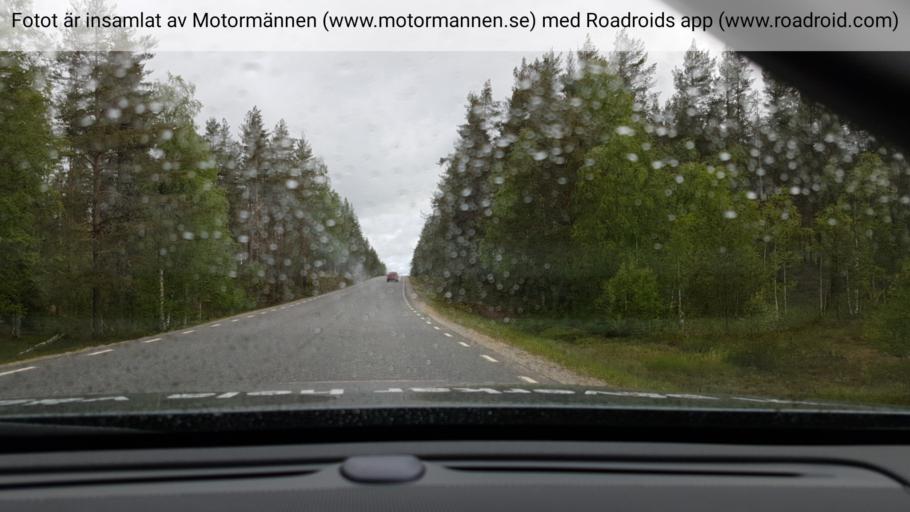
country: SE
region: Vaesterbotten
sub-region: Bjurholms Kommun
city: Bjurholm
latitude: 63.9760
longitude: 18.8156
